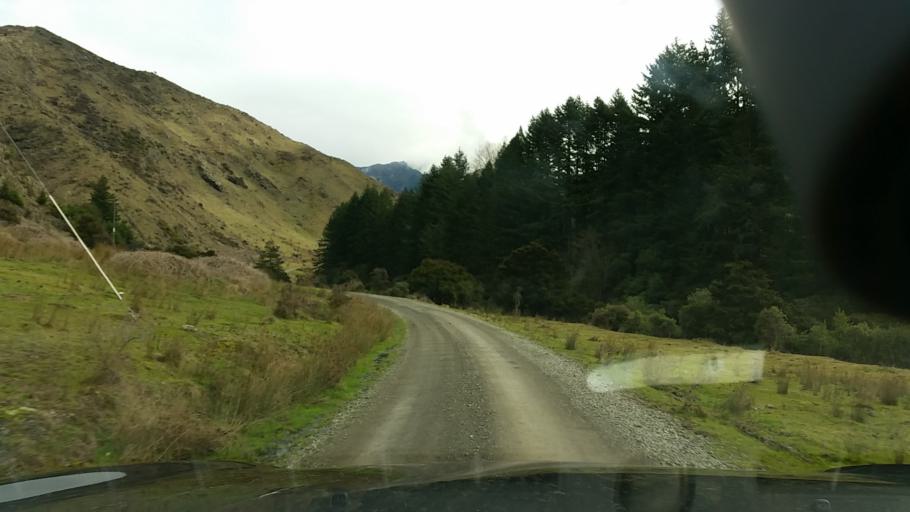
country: NZ
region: Tasman
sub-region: Tasman District
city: Richmond
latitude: -41.7311
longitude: 173.4557
